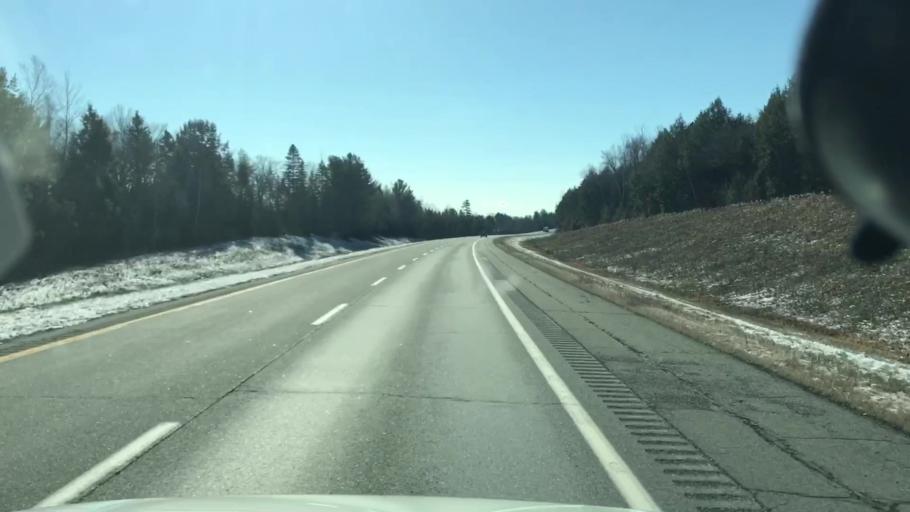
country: US
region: Maine
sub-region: Penobscot County
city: Howland
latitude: 45.2909
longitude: -68.6657
